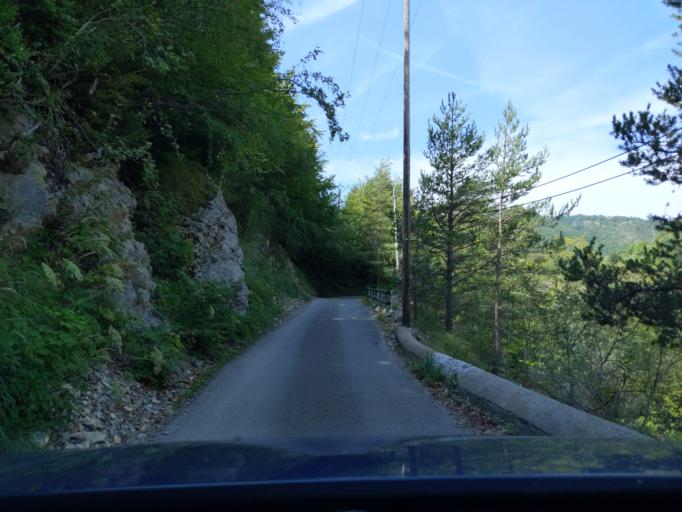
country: FR
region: Provence-Alpes-Cote d'Azur
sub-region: Departement des Hautes-Alpes
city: Veynes
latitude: 44.6330
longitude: 5.6659
